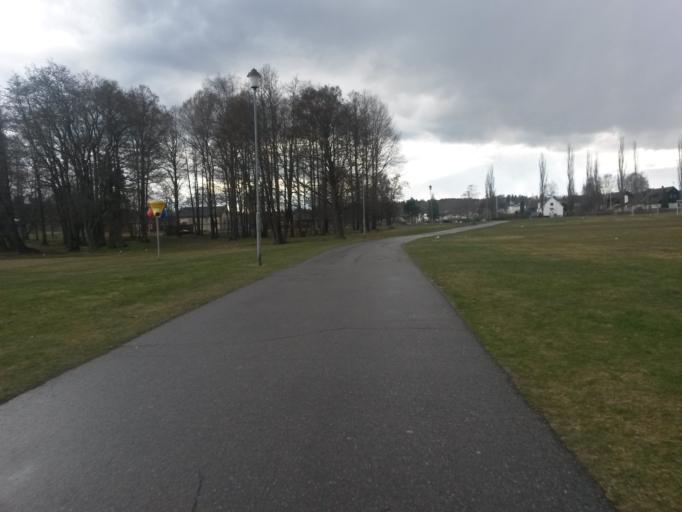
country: SE
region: OErebro
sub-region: Karlskoga Kommun
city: Karlskoga
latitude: 59.3215
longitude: 14.5261
